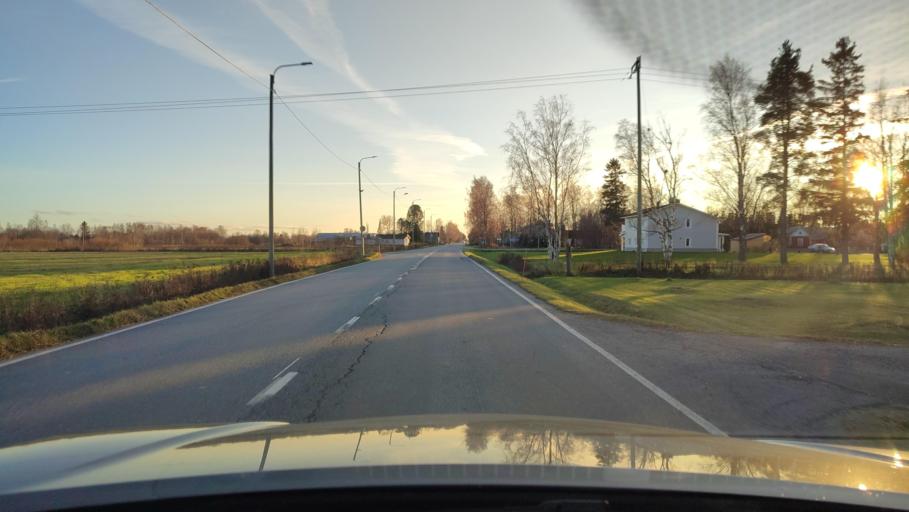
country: FI
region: Ostrobothnia
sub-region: Sydosterbotten
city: Naerpes
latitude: 62.6022
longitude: 21.4564
